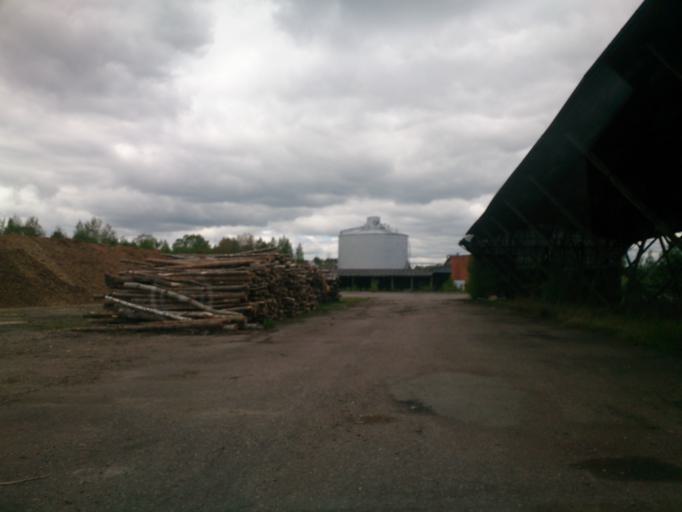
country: SE
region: OEstergoetland
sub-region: Atvidabergs Kommun
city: Atvidaberg
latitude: 58.2006
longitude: 16.0092
